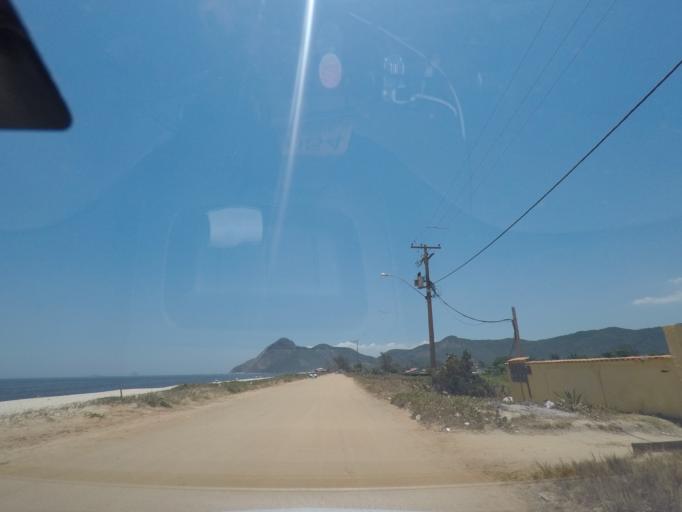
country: BR
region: Rio de Janeiro
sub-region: Niteroi
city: Niteroi
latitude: -22.9692
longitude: -42.9767
